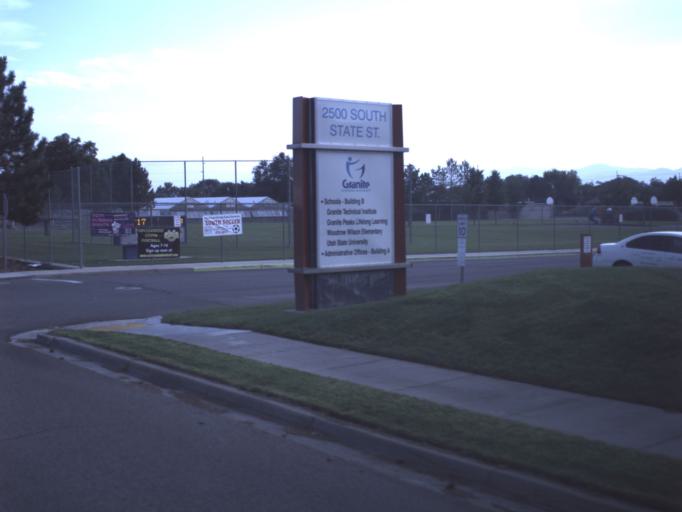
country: US
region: Utah
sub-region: Salt Lake County
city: South Salt Lake
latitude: 40.7153
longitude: -111.8884
